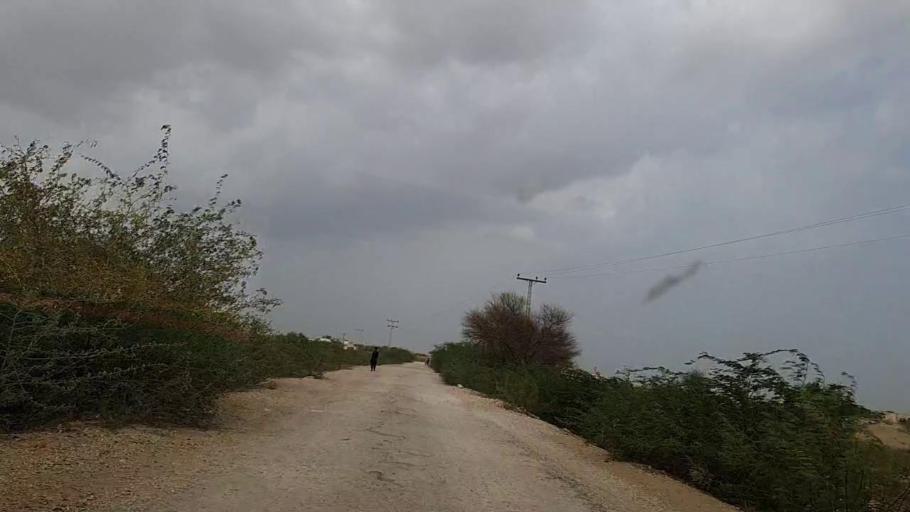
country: PK
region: Sindh
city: Kotri
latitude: 25.2868
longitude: 68.2131
